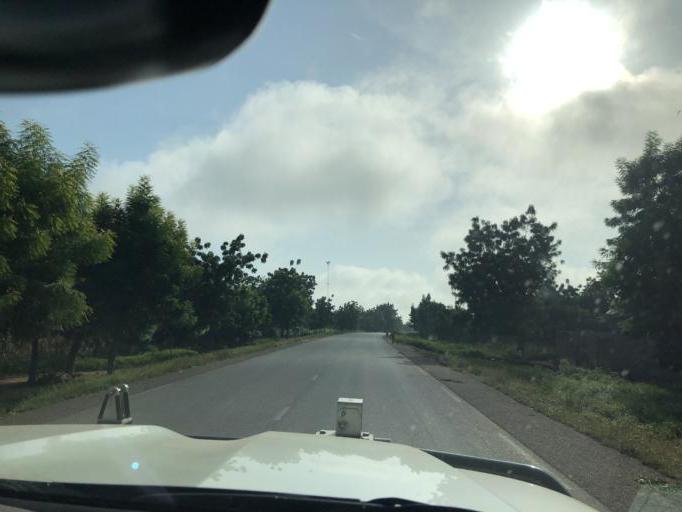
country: CM
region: North Province
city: Pitoa
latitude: 9.4942
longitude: 13.6925
